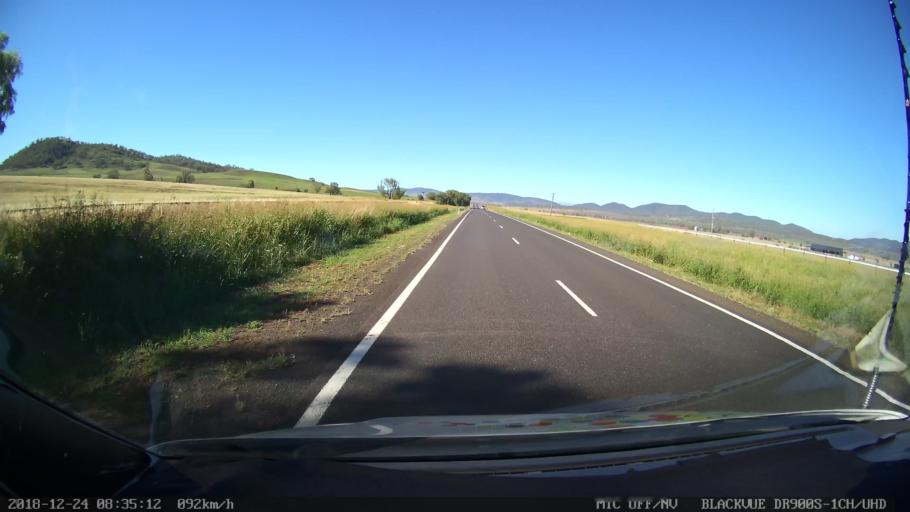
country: AU
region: New South Wales
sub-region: Liverpool Plains
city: Quirindi
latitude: -31.2996
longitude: 150.6612
